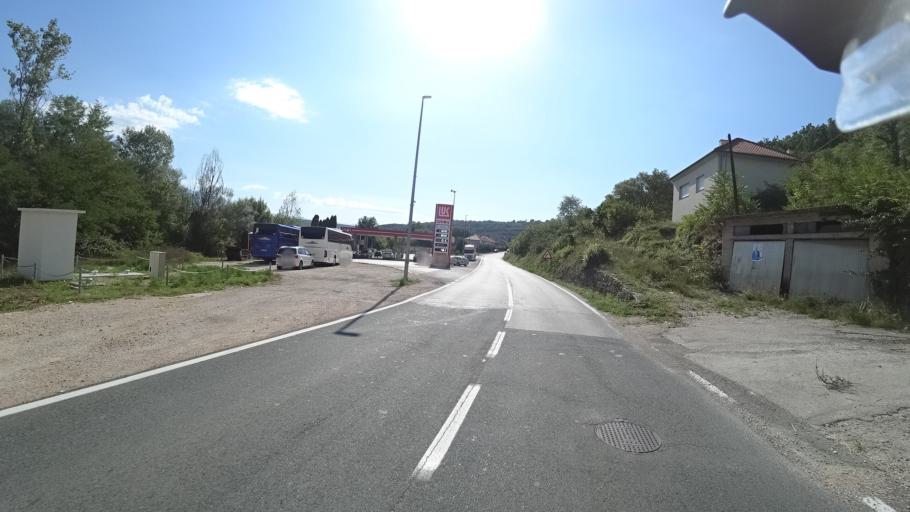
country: HR
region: Sibensko-Kniniska
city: Knin
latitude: 44.0304
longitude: 16.1906
